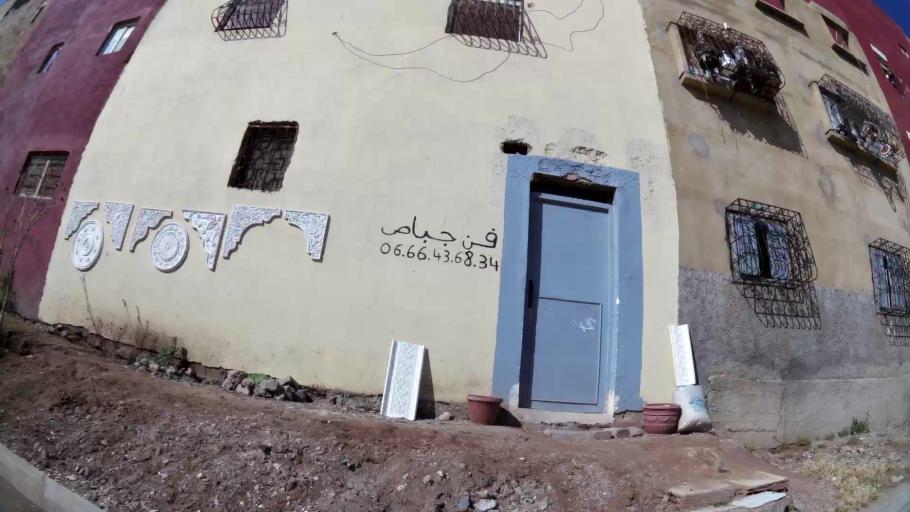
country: MA
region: Rabat-Sale-Zemmour-Zaer
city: Sale
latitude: 34.0595
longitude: -6.8105
